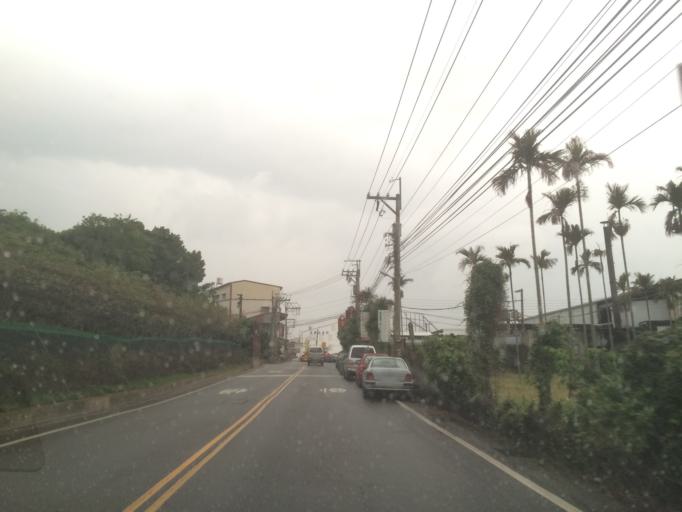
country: TW
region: Taiwan
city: Fengyuan
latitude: 24.1890
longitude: 120.8131
